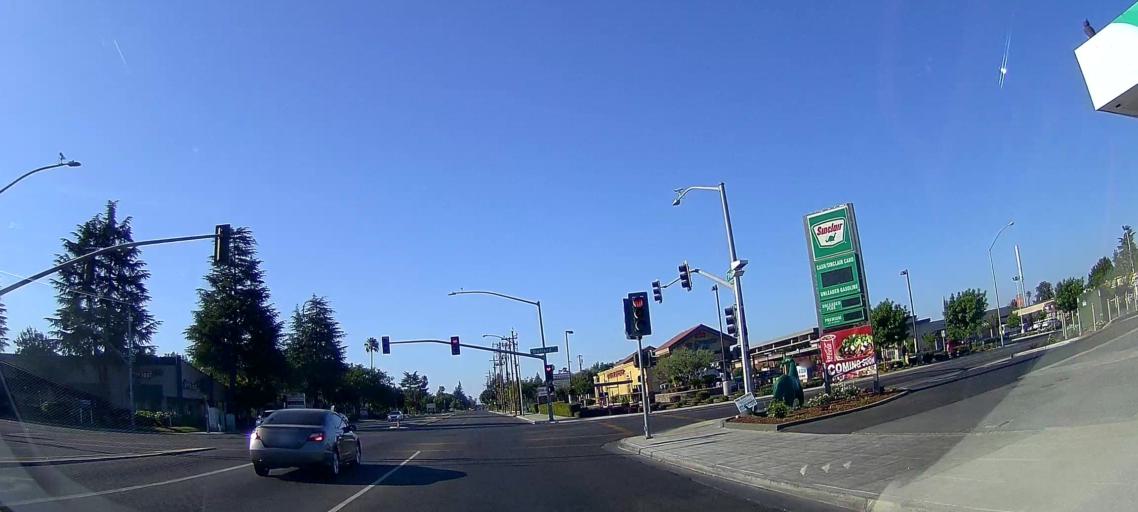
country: US
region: California
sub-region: Fresno County
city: Fresno
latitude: 36.8225
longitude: -119.8082
